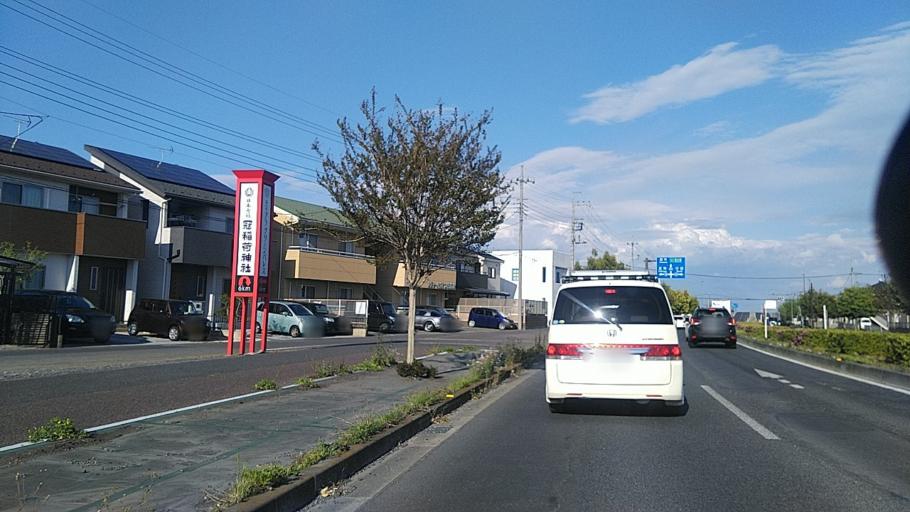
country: JP
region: Gunma
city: Ota
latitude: 36.2709
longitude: 139.4159
